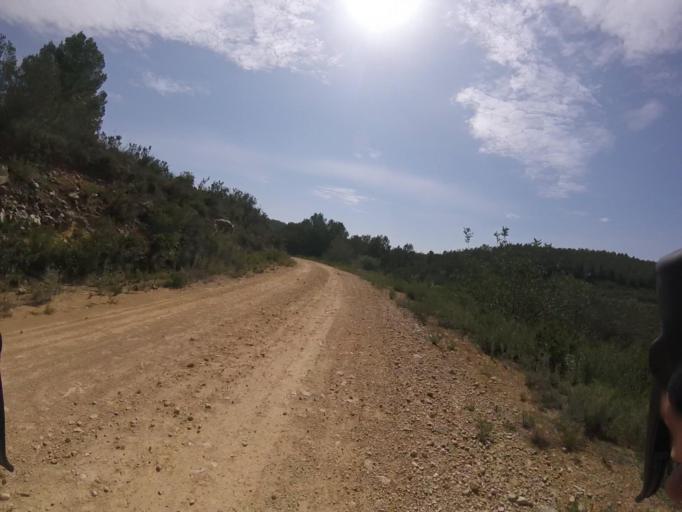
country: ES
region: Valencia
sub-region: Provincia de Castello
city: Cuevas de Vinroma
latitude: 40.2924
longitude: 0.1258
